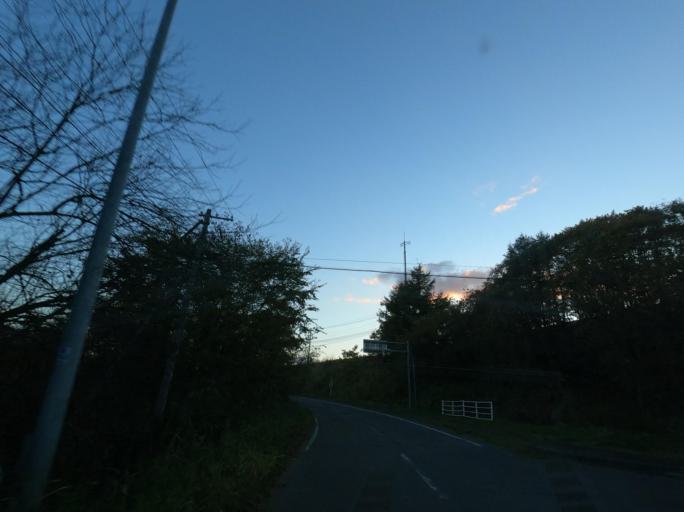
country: JP
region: Hokkaido
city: Kushiro
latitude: 43.2196
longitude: 144.4304
